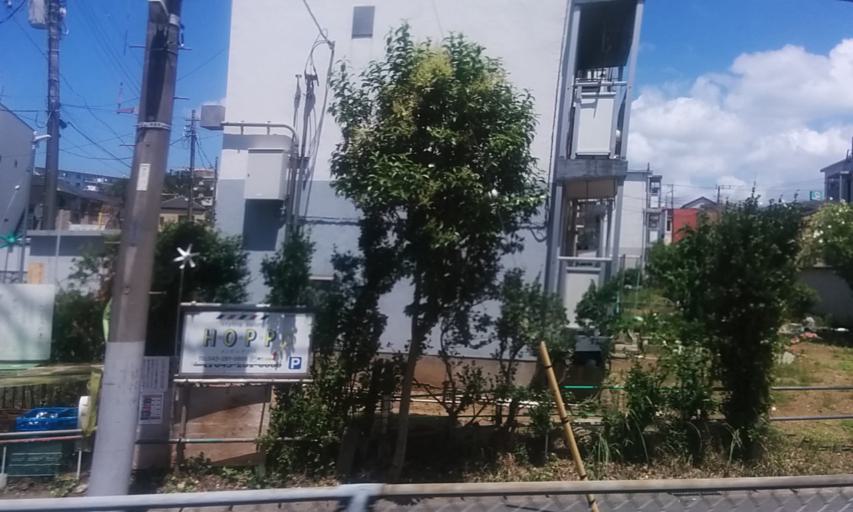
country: JP
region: Chiba
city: Chiba
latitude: 35.5756
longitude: 140.1363
